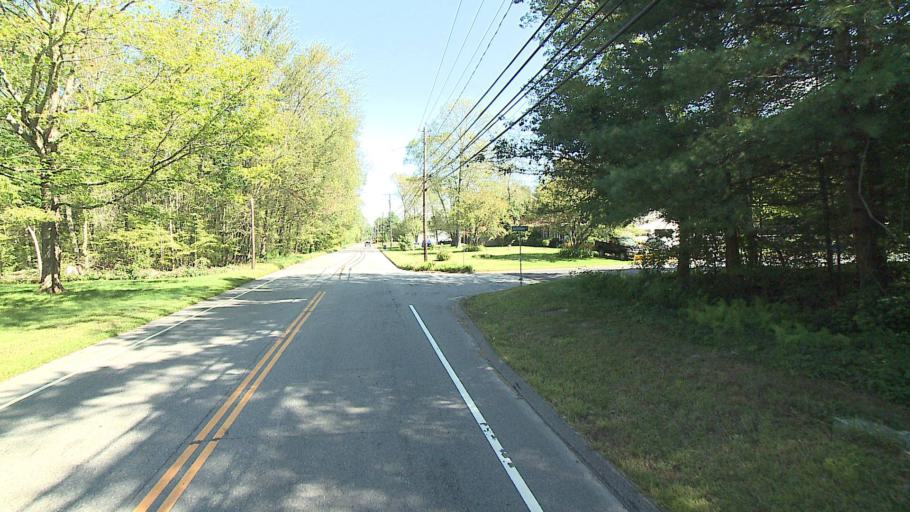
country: US
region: Connecticut
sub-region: Windham County
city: East Brooklyn
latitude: 41.7725
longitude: -71.8970
